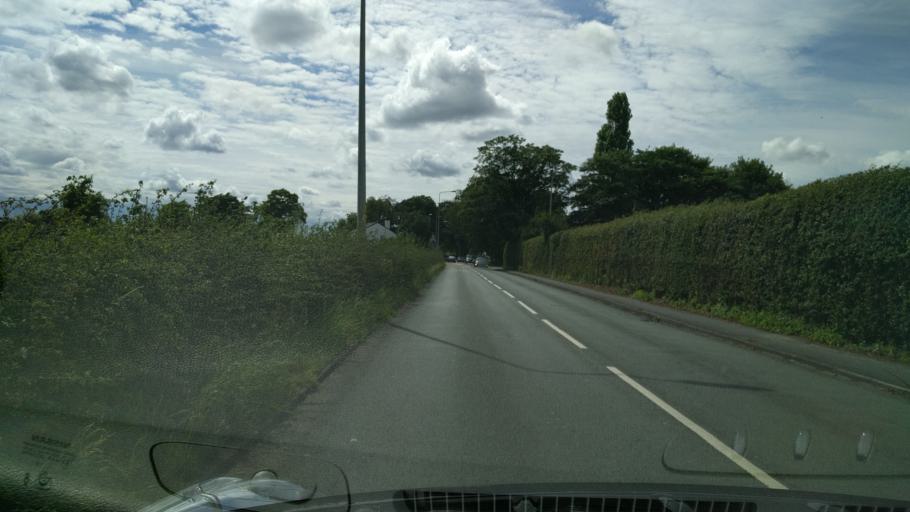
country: GB
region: England
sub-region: Warrington
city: Culcheth
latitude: 53.4564
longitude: -2.5050
